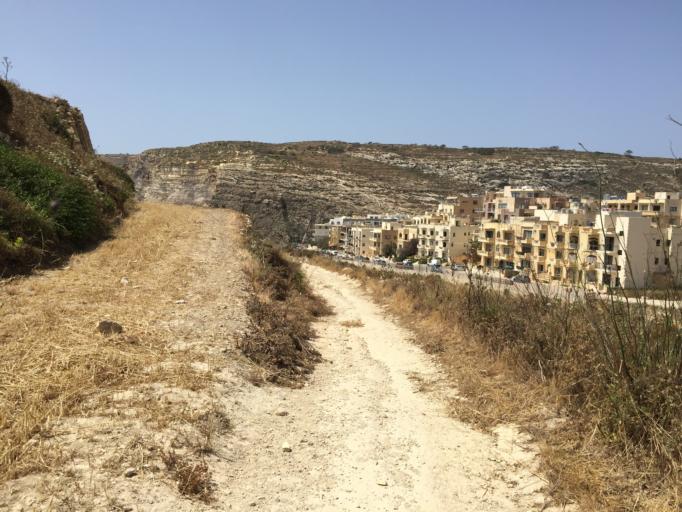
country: MT
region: Il-Munxar
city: Munxar
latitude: 36.0257
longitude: 14.2177
